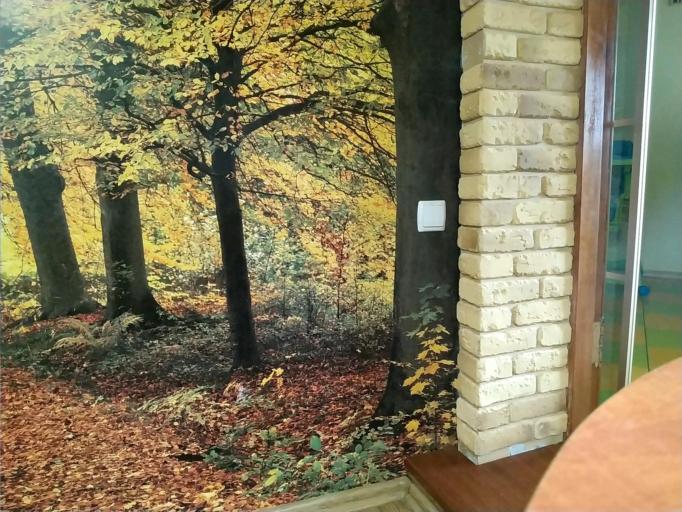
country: RU
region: Smolensk
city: Dorogobuzh
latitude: 54.9562
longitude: 33.2847
